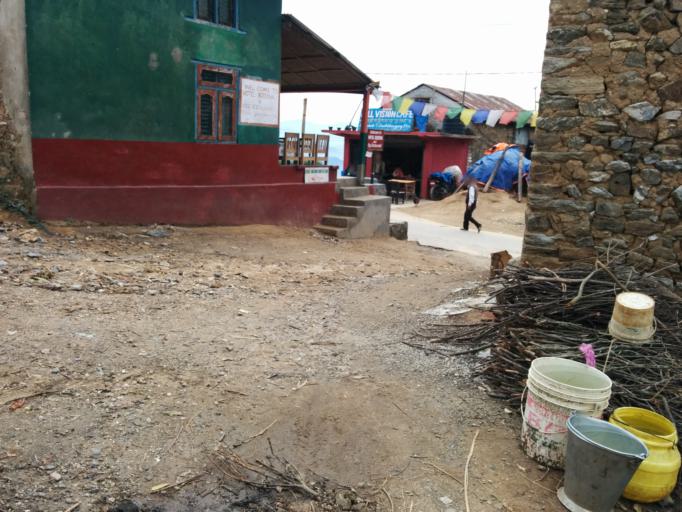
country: NP
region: Central Region
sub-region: Bagmati Zone
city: Nagarkot
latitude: 27.7641
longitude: 85.4979
